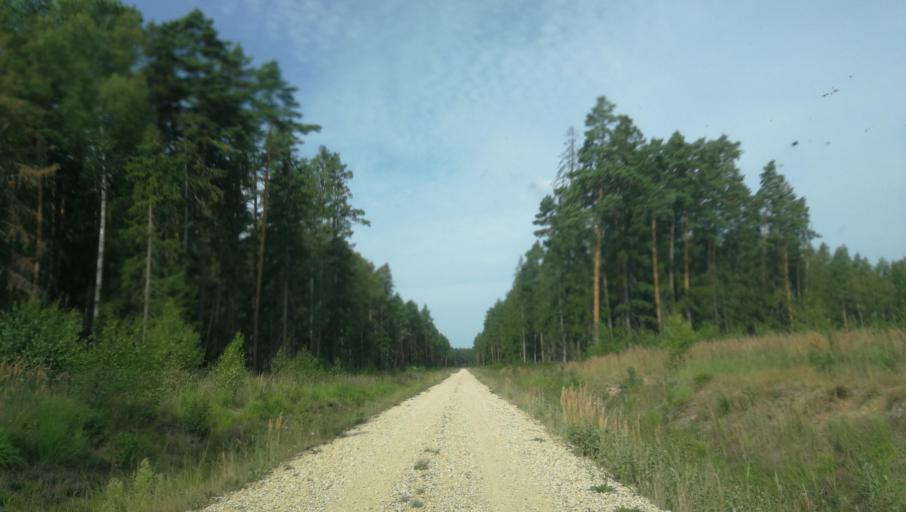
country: LV
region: Pavilostas
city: Pavilosta
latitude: 56.8156
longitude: 21.3326
